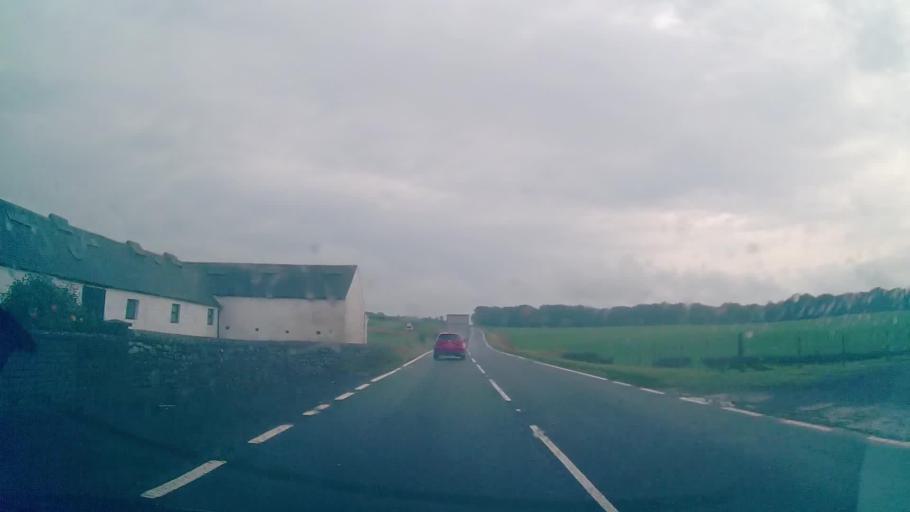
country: GB
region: Scotland
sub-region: Dumfries and Galloway
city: Lochmaben
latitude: 55.0431
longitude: -3.4461
